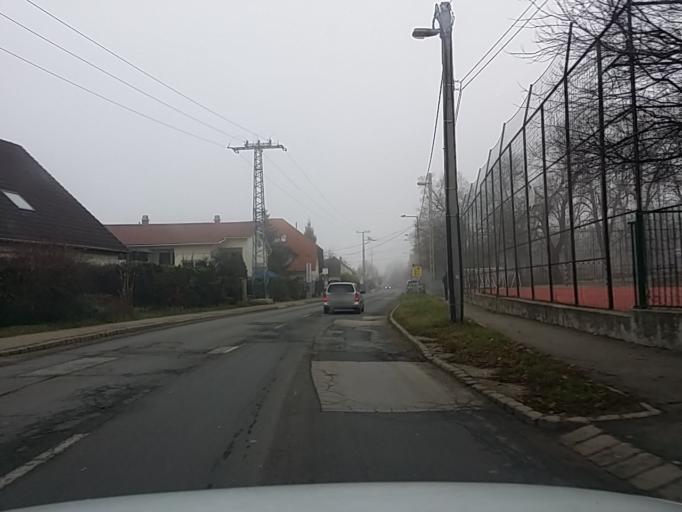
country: HU
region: Pest
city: Budakeszi
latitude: 47.5122
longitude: 18.9272
